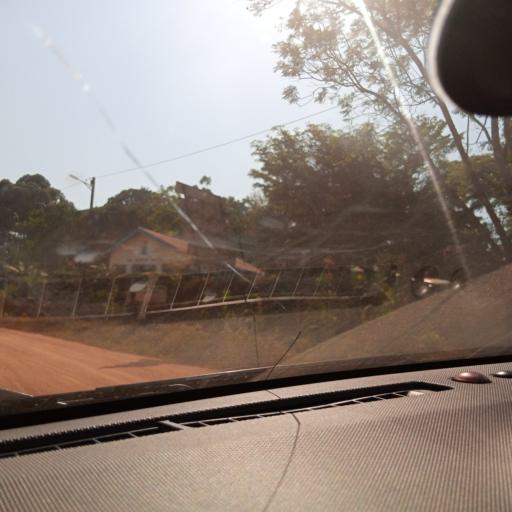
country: UG
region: Central Region
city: Masaka
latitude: -0.3327
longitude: 31.7351
